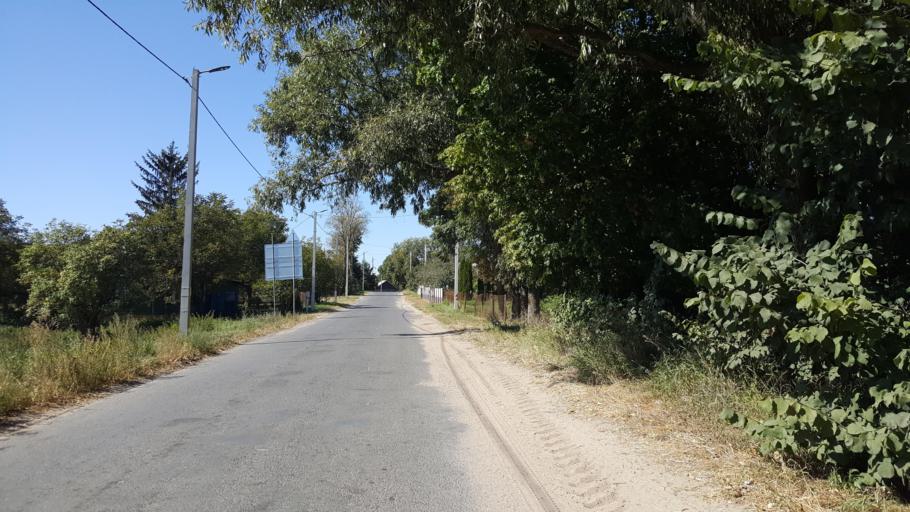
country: BY
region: Brest
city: Vysokaye
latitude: 52.2212
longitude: 23.4462
